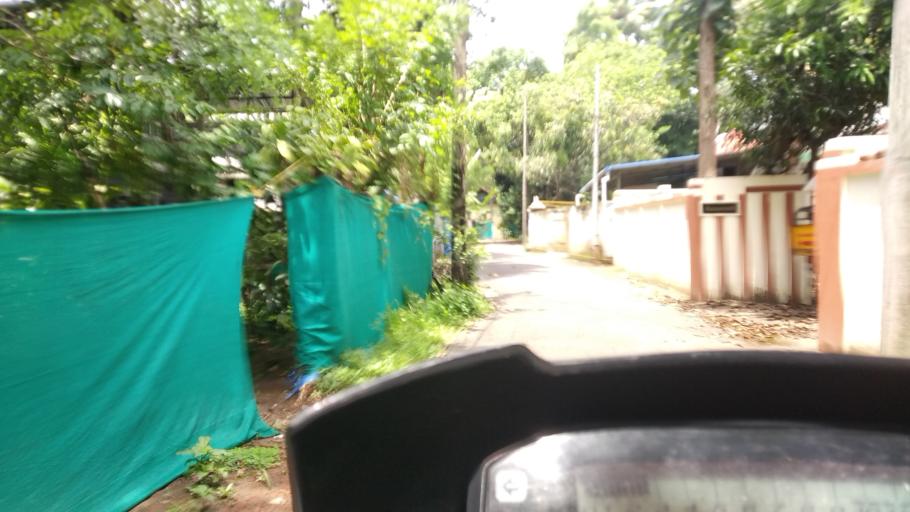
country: IN
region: Kerala
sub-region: Ernakulam
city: Elur
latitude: 10.0645
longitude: 76.2089
